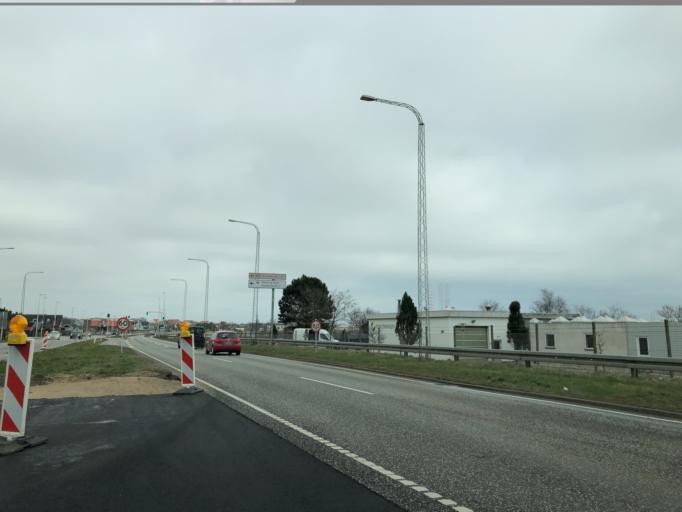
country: DK
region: North Denmark
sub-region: Frederikshavn Kommune
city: Frederikshavn
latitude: 57.4255
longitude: 10.5245
